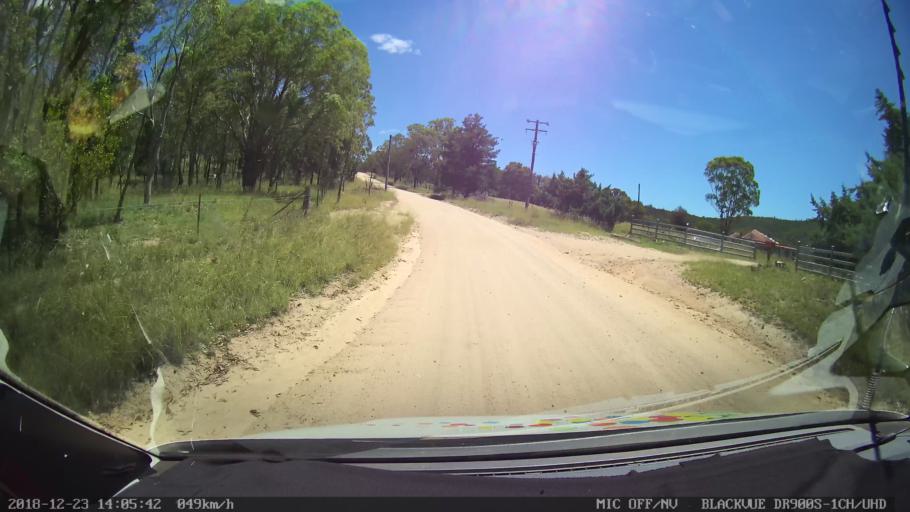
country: AU
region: New South Wales
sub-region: Tamworth Municipality
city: Manilla
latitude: -30.6258
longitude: 151.0788
